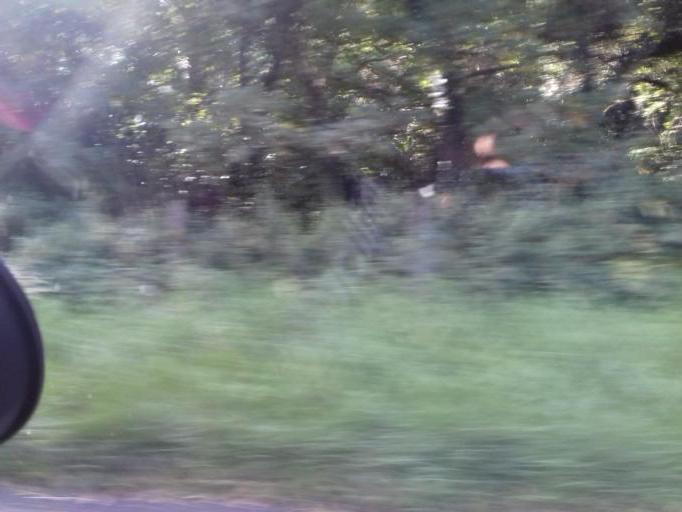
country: IE
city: Kentstown
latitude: 53.6391
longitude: -6.4972
